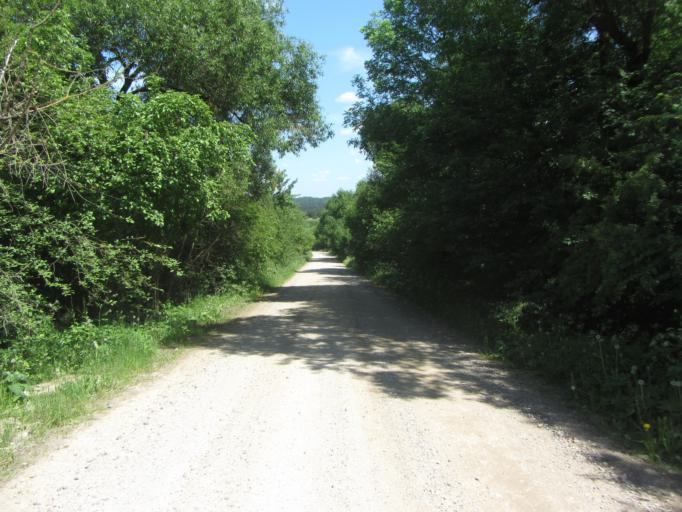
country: LT
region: Vilnius County
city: Elektrenai
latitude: 54.9372
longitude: 24.6696
